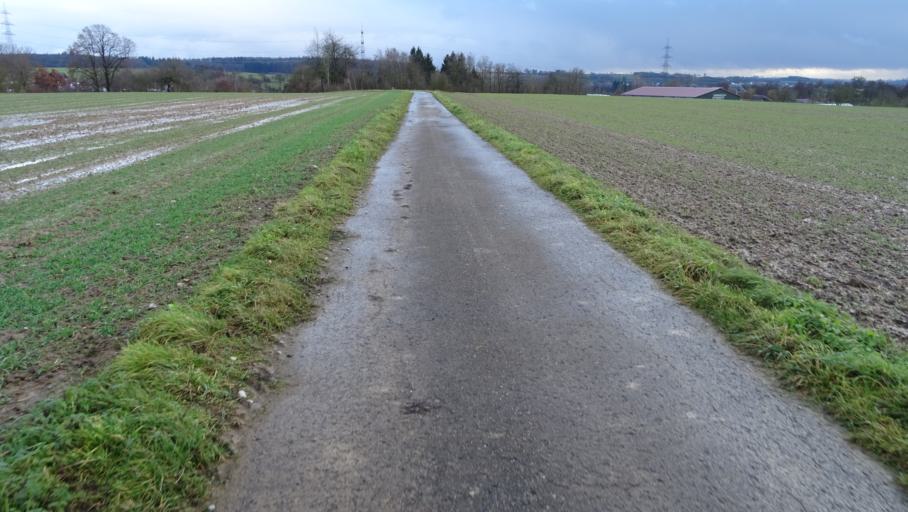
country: DE
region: Baden-Wuerttemberg
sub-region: Karlsruhe Region
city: Seckach
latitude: 49.4329
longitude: 9.2874
